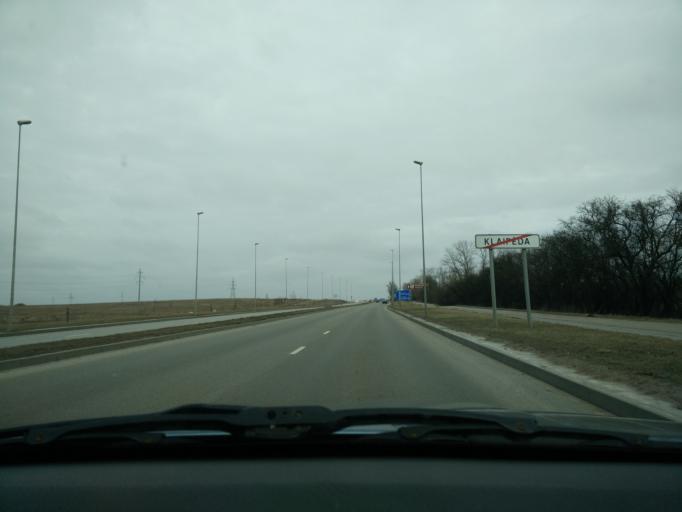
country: LT
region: Klaipedos apskritis
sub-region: Klaipeda
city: Klaipeda
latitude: 55.7280
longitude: 21.1745
